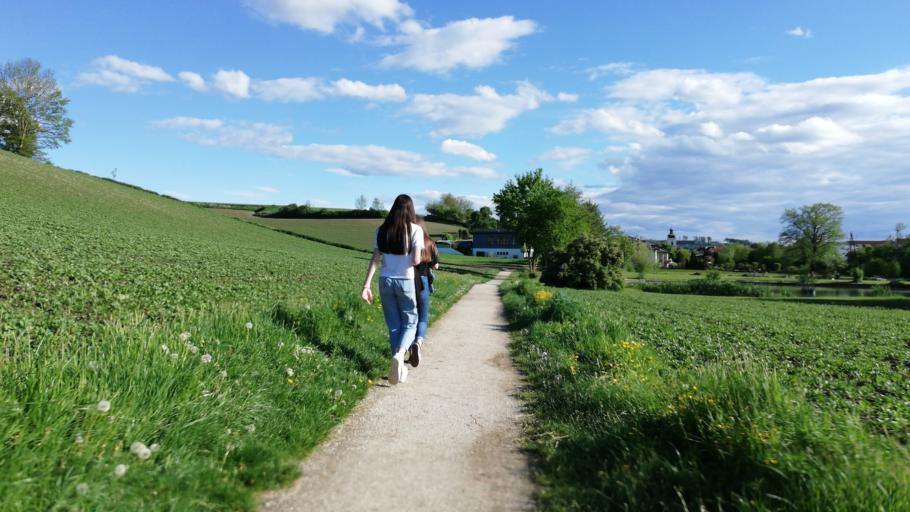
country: AT
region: Upper Austria
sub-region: Politischer Bezirk Grieskirchen
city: Bad Schallerbach
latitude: 48.2095
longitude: 13.9570
